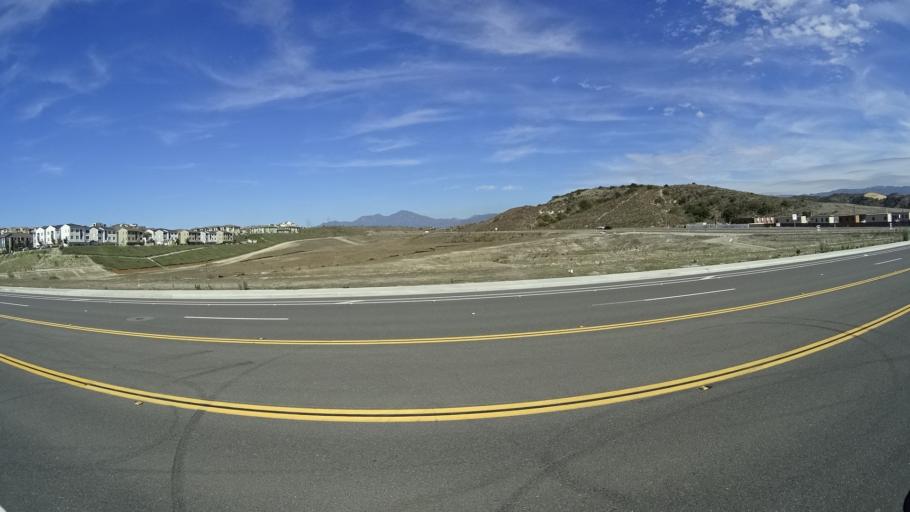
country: US
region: California
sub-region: Orange County
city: Ladera Ranch
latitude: 33.5267
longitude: -117.5990
